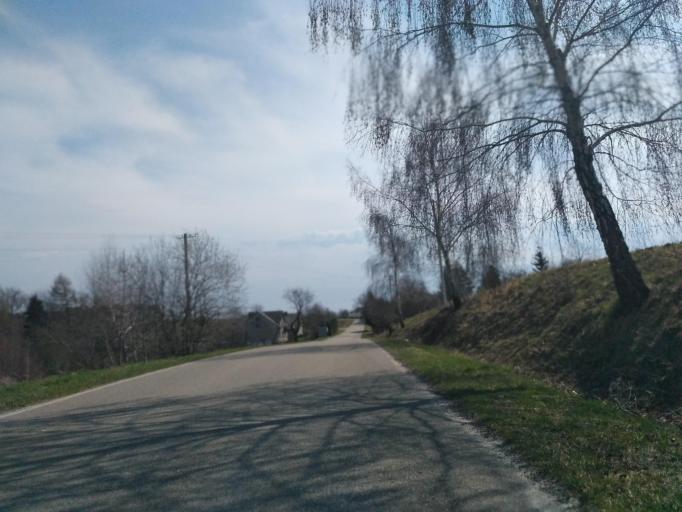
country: PL
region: Subcarpathian Voivodeship
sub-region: Powiat ropczycko-sedziszowski
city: Iwierzyce
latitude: 49.9777
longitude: 21.7455
